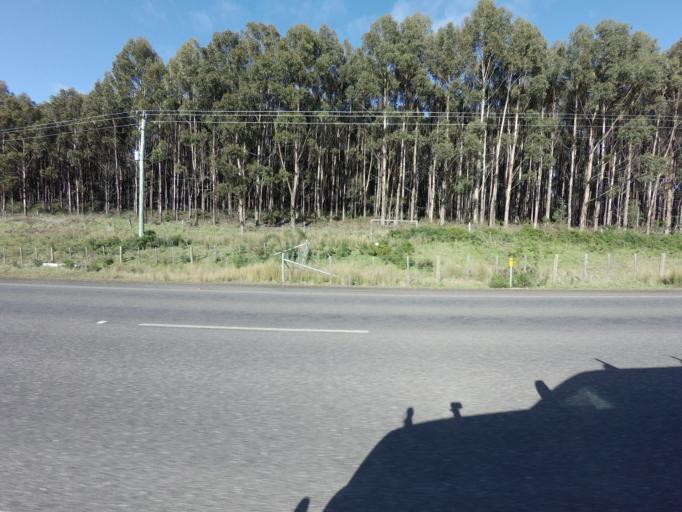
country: AU
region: Tasmania
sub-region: Huon Valley
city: Geeveston
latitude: -43.2574
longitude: 147.0039
